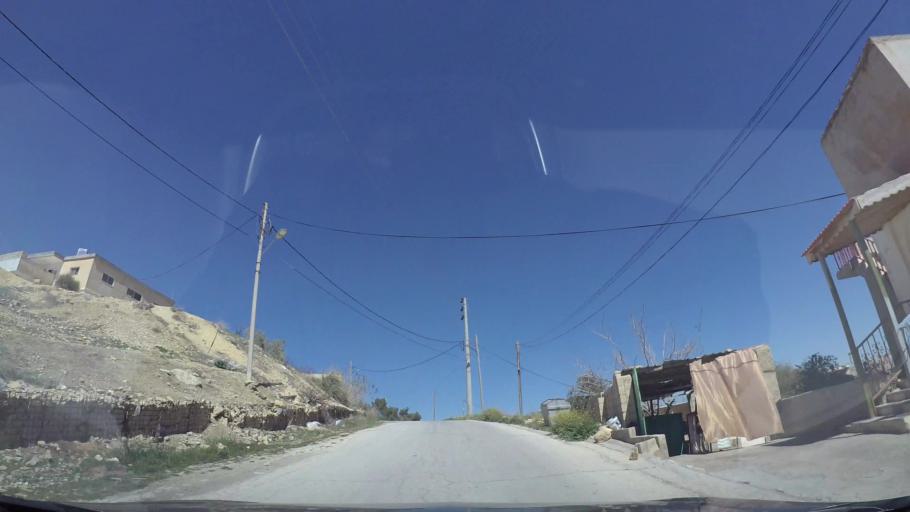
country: JO
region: Tafielah
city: At Tafilah
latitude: 30.8372
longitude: 35.5750
